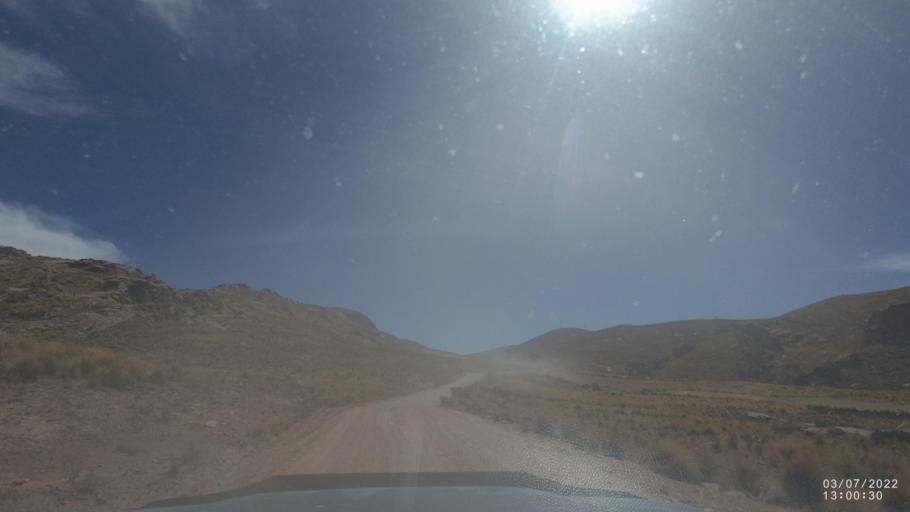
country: BO
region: Cochabamba
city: Colchani
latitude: -17.7139
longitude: -66.6893
